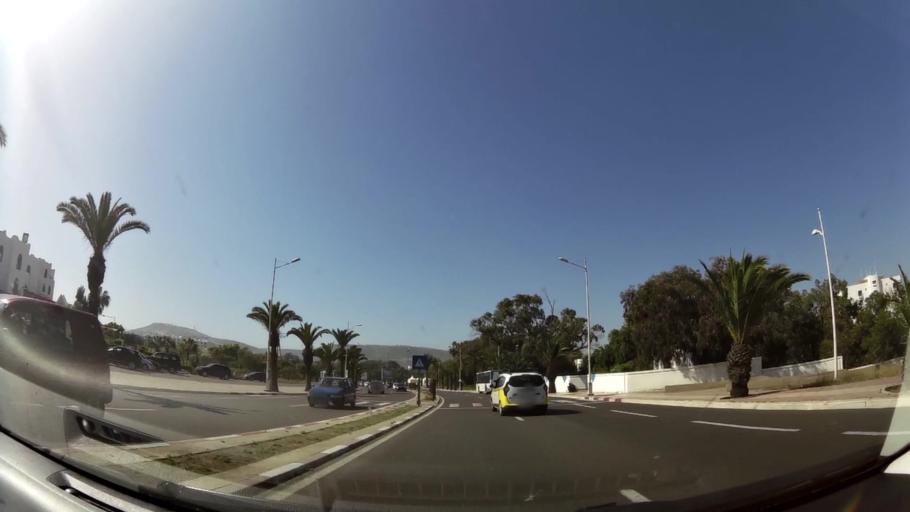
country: MA
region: Souss-Massa-Draa
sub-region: Agadir-Ida-ou-Tnan
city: Agadir
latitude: 30.4173
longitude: -9.5997
